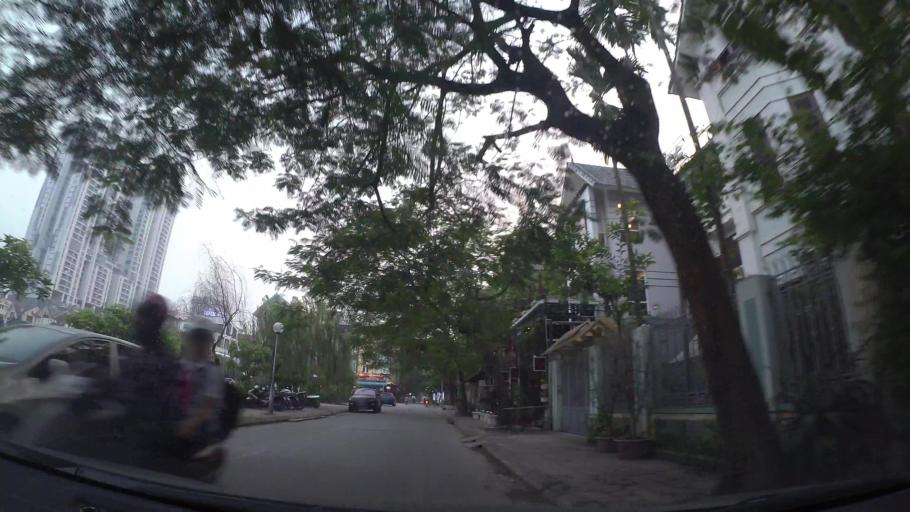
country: VN
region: Ha Noi
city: Ha Dong
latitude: 20.9792
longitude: 105.7901
